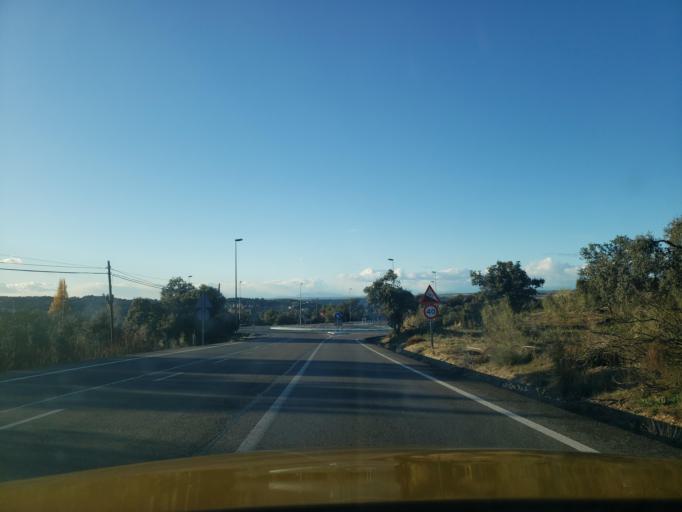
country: ES
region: Castille-La Mancha
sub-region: Province of Toledo
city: Toledo
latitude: 39.8452
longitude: -4.0222
